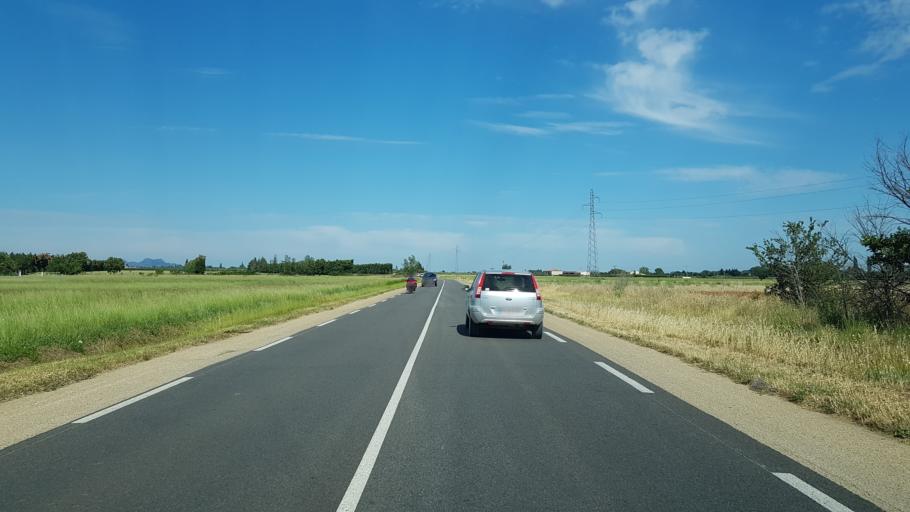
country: FR
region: Provence-Alpes-Cote d'Azur
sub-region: Departement des Bouches-du-Rhone
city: Paradou
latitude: 43.6691
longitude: 4.7531
